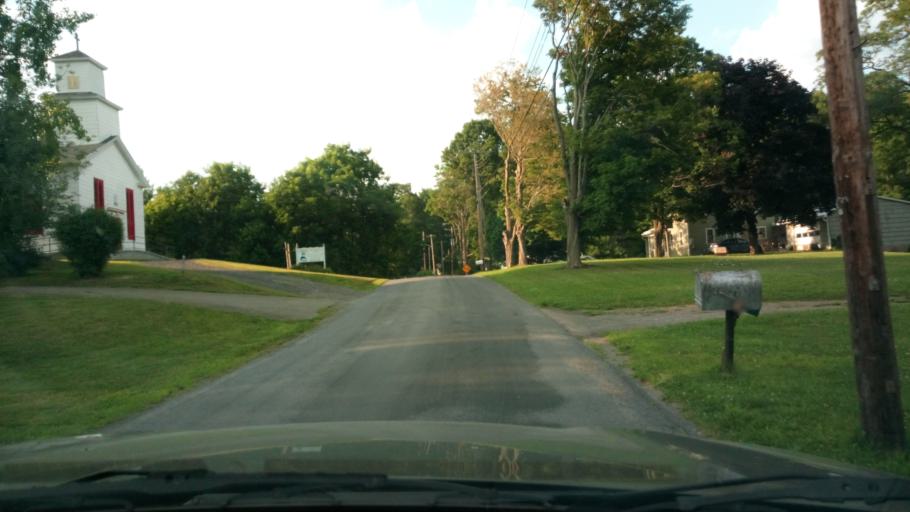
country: US
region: New York
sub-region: Wayne County
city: Lyons
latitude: 43.0791
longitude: -76.9461
